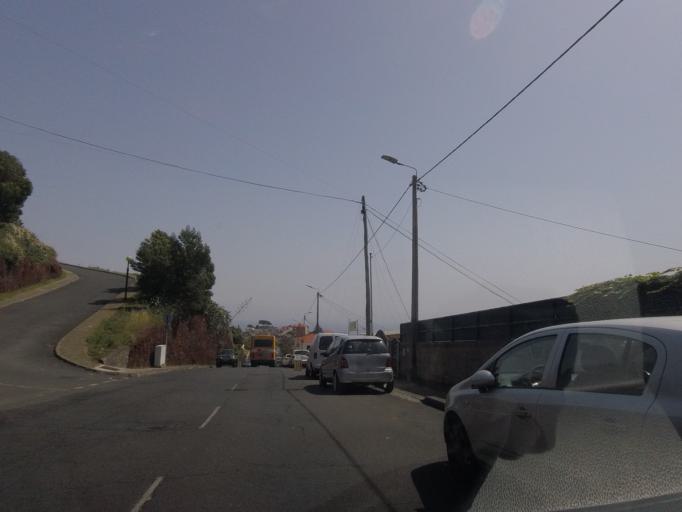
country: PT
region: Madeira
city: Camara de Lobos
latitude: 32.6617
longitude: -16.9464
